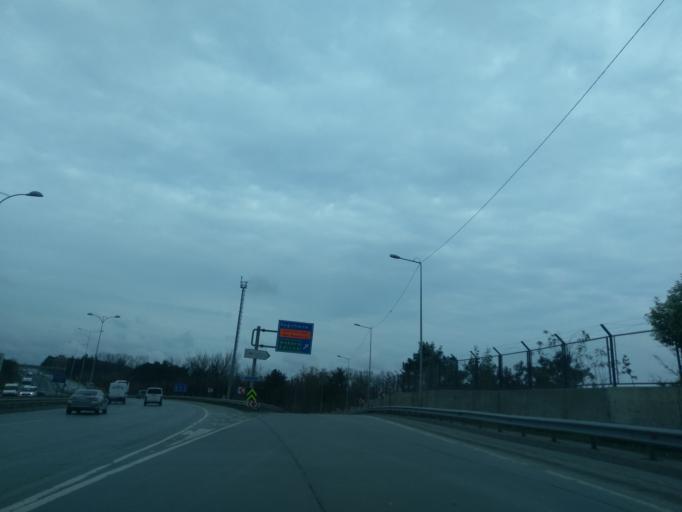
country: TR
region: Istanbul
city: Sisli
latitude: 41.1040
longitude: 28.9544
